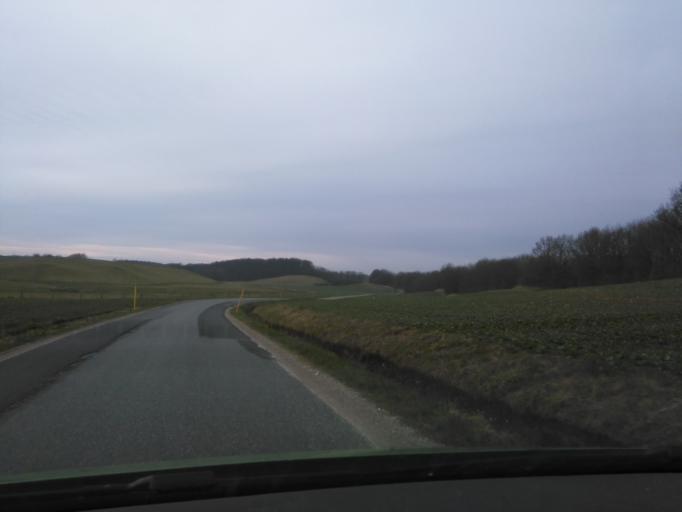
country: DK
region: Central Jutland
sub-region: Odder Kommune
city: Odder
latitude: 55.9262
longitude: 10.1004
